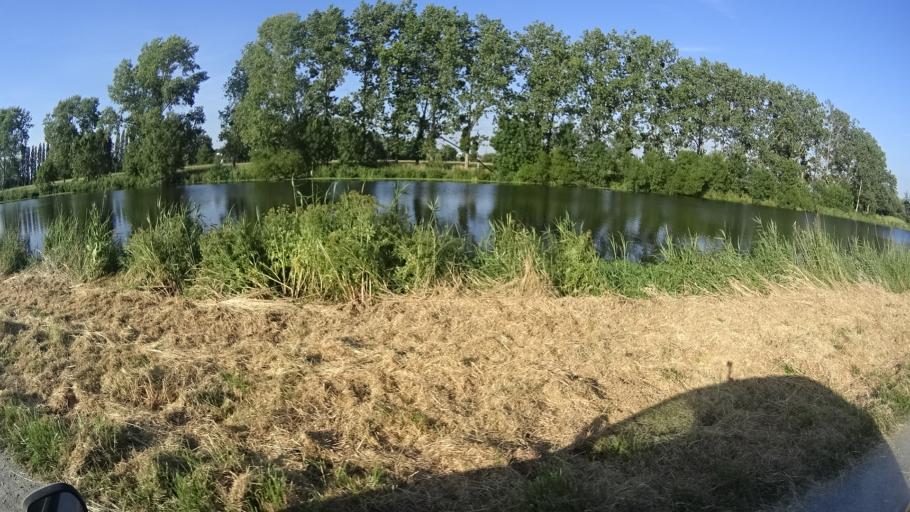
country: FR
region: Brittany
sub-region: Departement du Morbihan
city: Saint-Jean-la-Poterie
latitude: 47.6428
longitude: -2.1098
